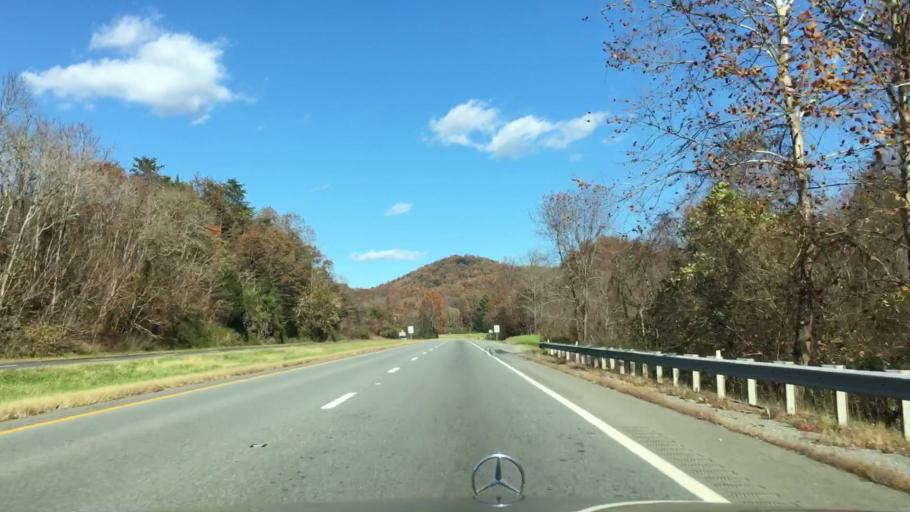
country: US
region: Virginia
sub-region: Albemarle County
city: Crozet
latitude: 37.9725
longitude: -78.6122
